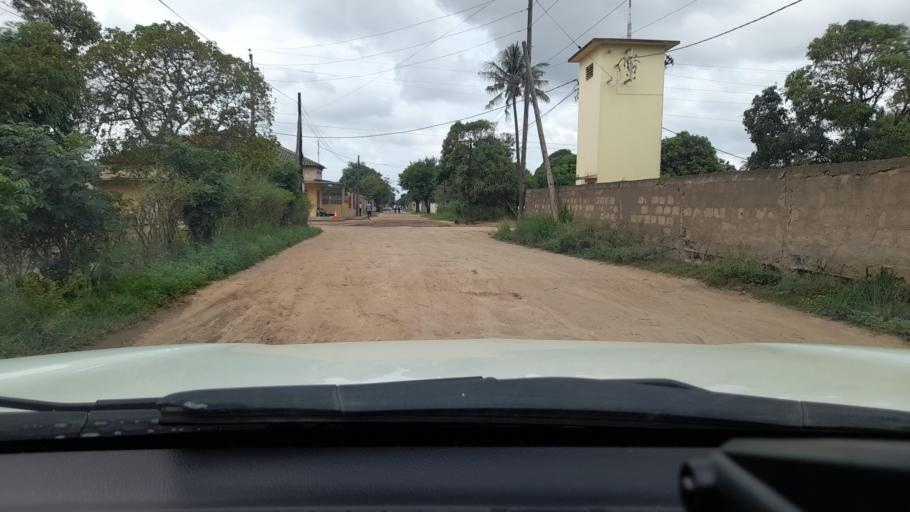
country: MZ
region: Maputo
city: Matola
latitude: -25.9034
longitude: 32.4890
